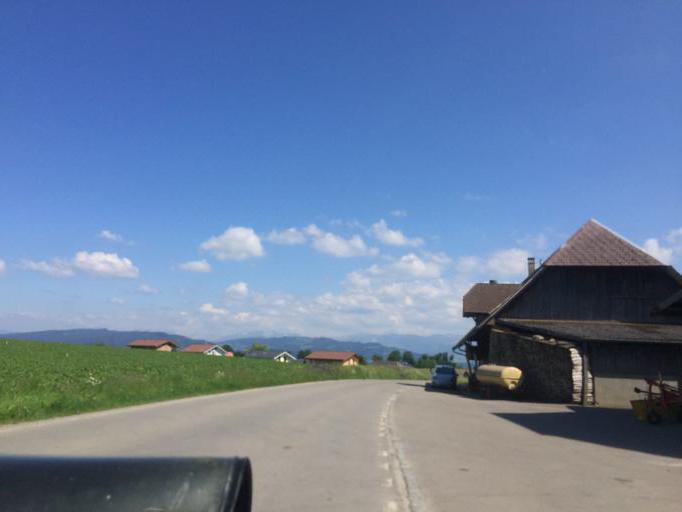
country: CH
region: Bern
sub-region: Bern-Mittelland District
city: Toffen
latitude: 46.8677
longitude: 7.5241
